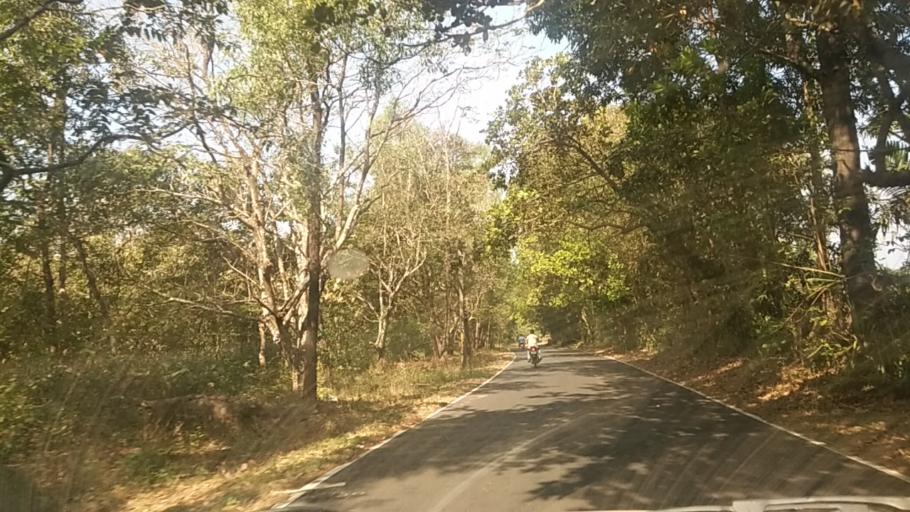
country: IN
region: Goa
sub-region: South Goa
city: Sanguem
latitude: 15.2072
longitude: 74.2198
